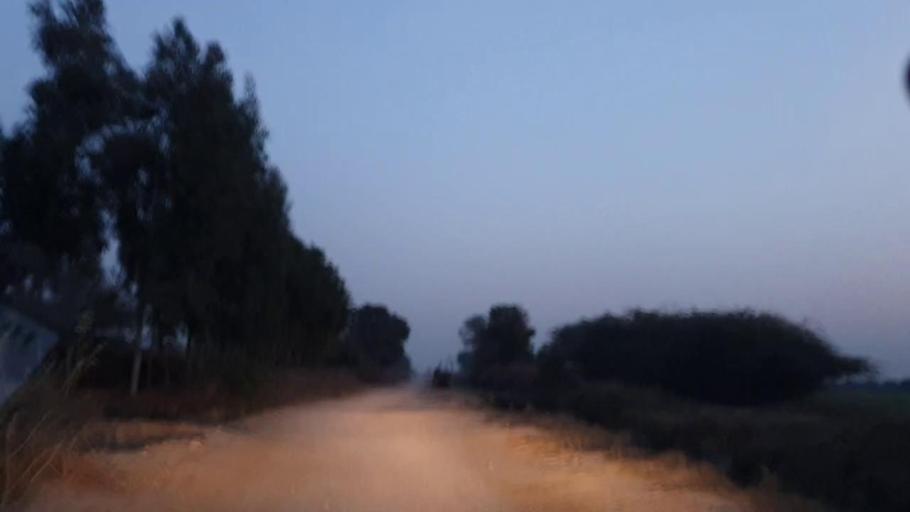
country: PK
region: Sindh
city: Tando Ghulam Ali
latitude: 25.1080
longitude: 68.9077
